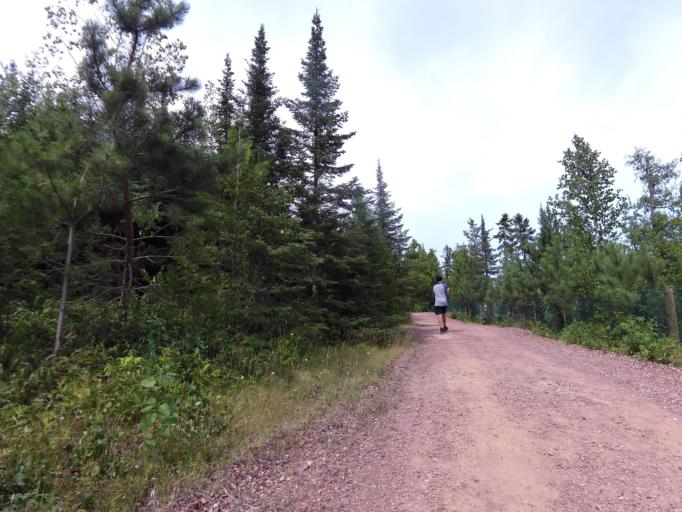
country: CA
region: Ontario
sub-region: Thunder Bay District
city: Thunder Bay
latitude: 48.8001
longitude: -88.6188
